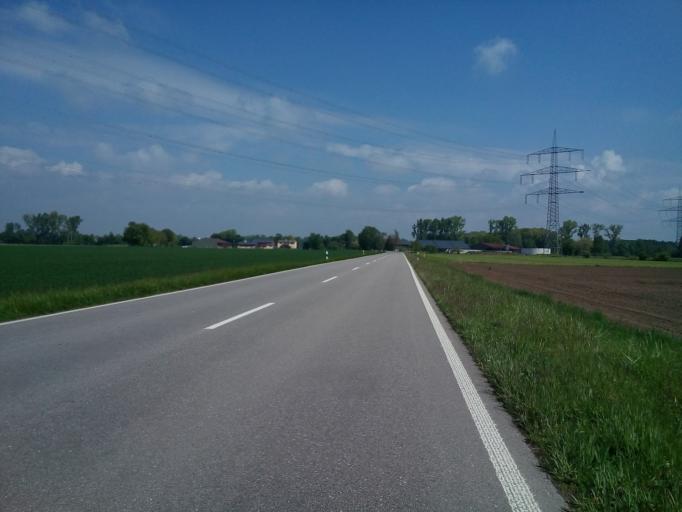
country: DE
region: Baden-Wuerttemberg
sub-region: Freiburg Region
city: Rheinau
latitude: 48.6654
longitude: 7.9939
